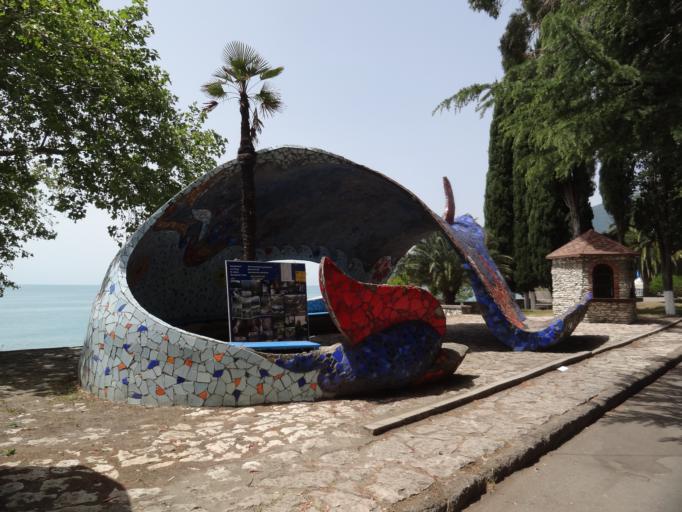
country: GE
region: Abkhazia
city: Gagra
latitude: 43.3010
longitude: 40.2562
